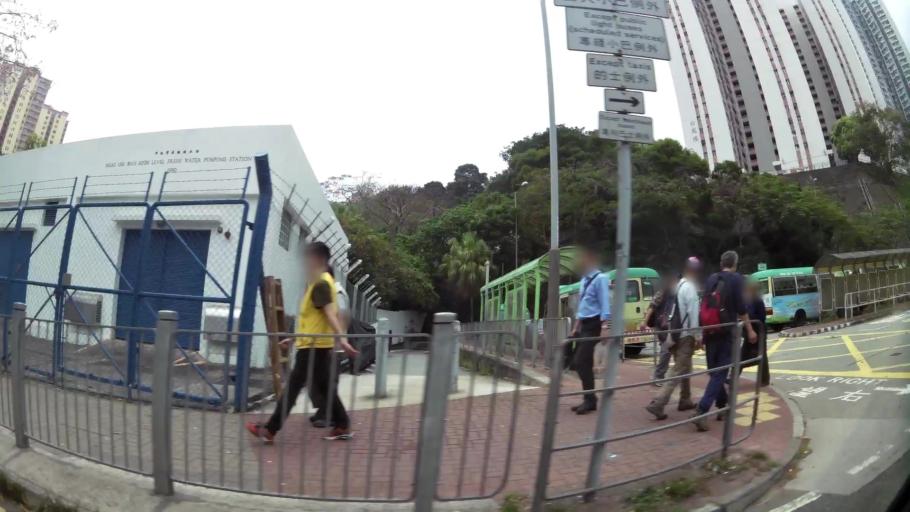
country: HK
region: Wong Tai Sin
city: Wong Tai Sin
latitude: 22.3345
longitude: 114.2113
